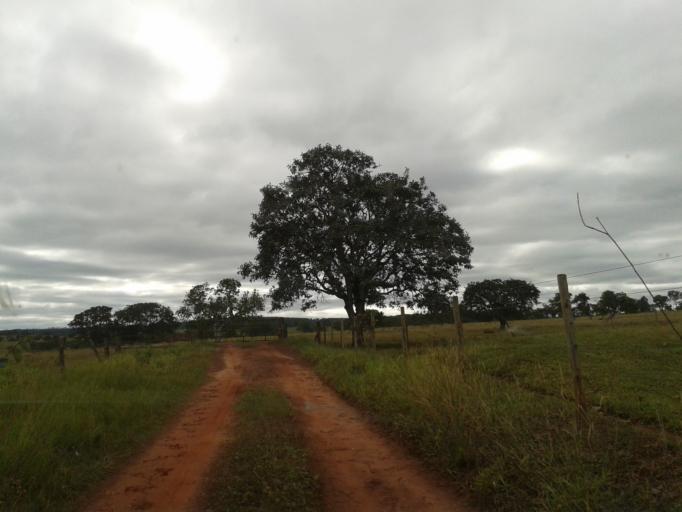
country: BR
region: Minas Gerais
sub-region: Campina Verde
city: Campina Verde
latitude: -19.5036
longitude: -49.6635
